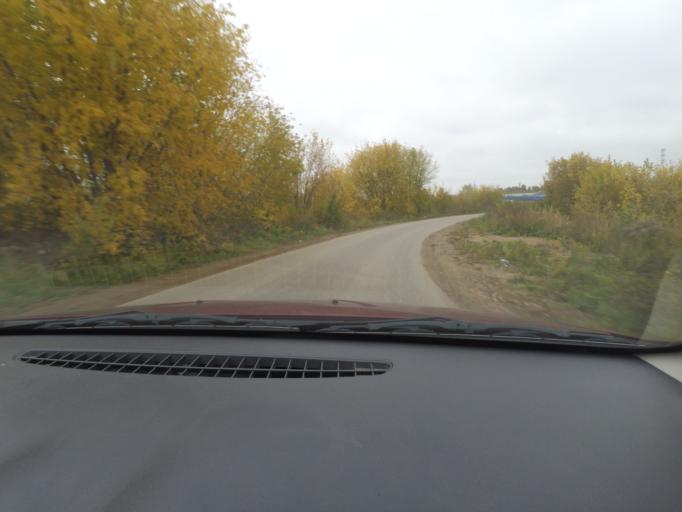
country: RU
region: Nizjnij Novgorod
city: Afonino
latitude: 56.2780
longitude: 44.0521
